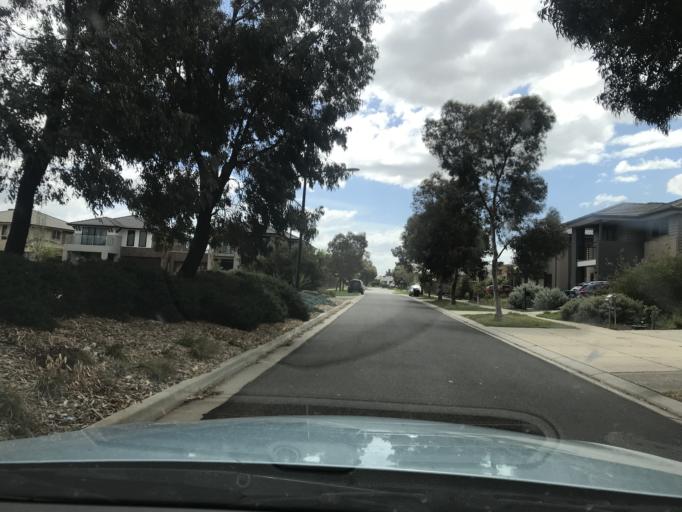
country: AU
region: Victoria
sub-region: Wyndham
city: Williams Landing
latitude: -37.8606
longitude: 144.7459
